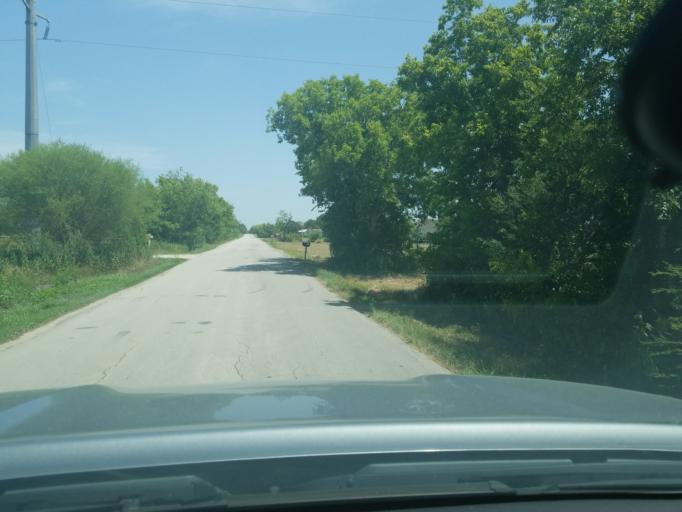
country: US
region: Texas
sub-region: Guadalupe County
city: Cibolo
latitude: 29.5827
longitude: -98.1999
